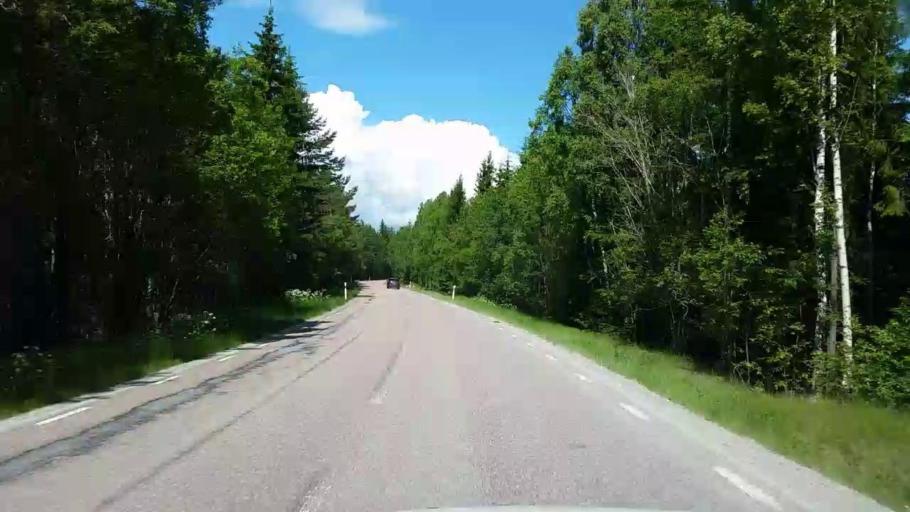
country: SE
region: Vaestmanland
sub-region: Fagersta Kommun
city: Fagersta
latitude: 59.9555
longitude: 15.7833
